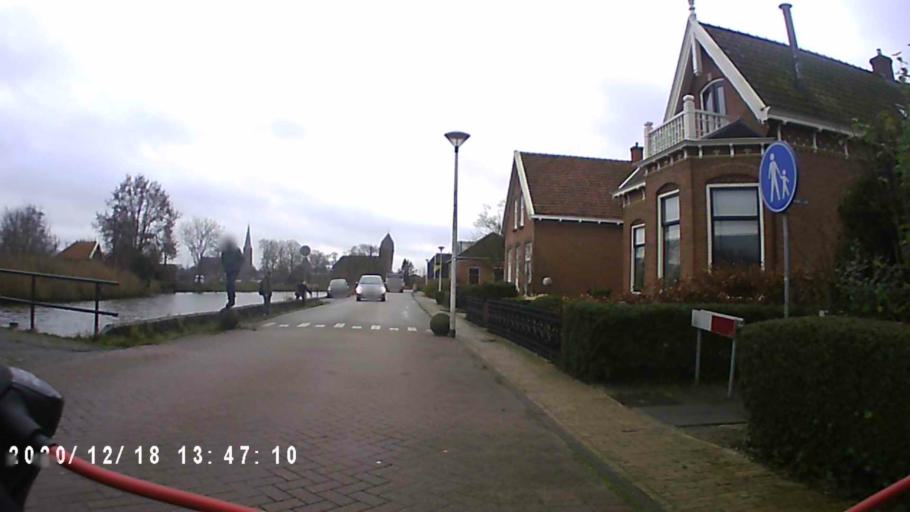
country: NL
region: Groningen
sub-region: Gemeente Bedum
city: Bedum
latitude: 53.3050
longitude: 6.6017
